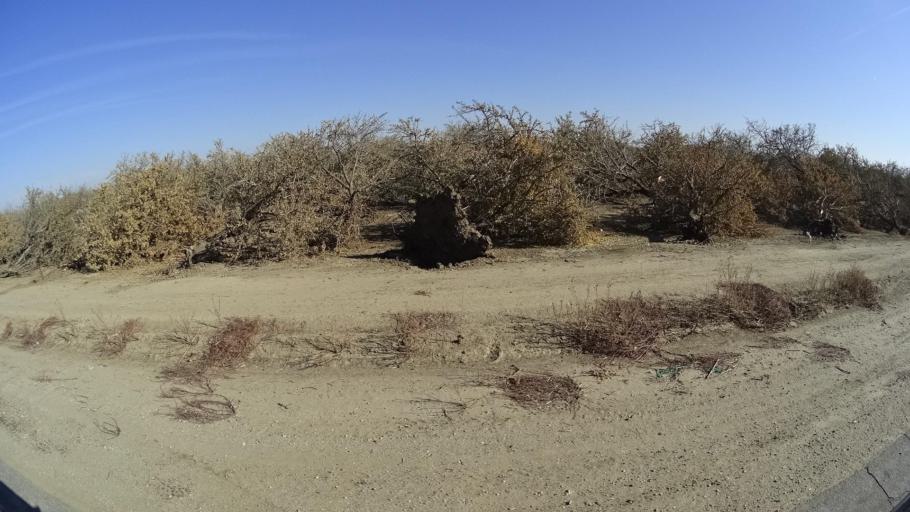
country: US
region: California
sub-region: Kern County
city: Wasco
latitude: 35.6641
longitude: -119.3485
